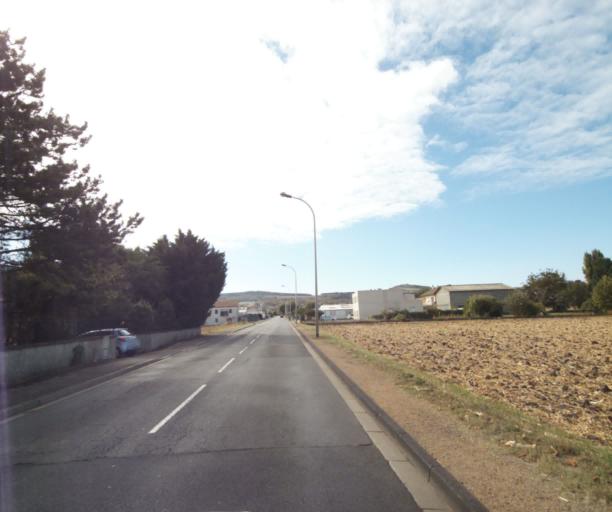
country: FR
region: Auvergne
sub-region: Departement du Puy-de-Dome
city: Aulnat
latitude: 45.7786
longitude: 3.1926
